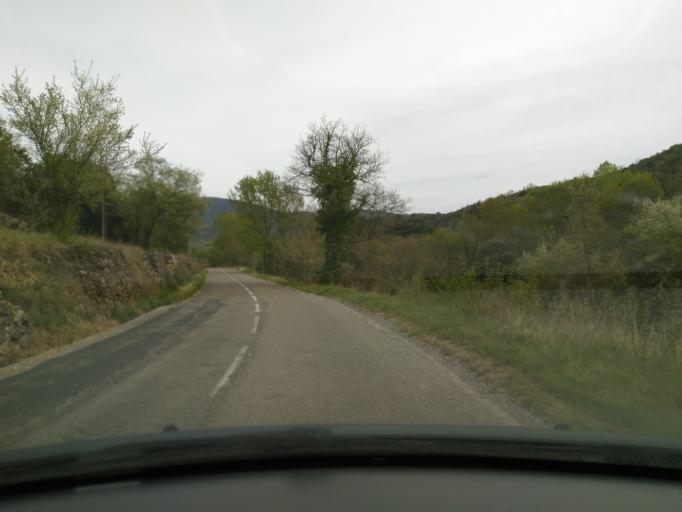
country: FR
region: Rhone-Alpes
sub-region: Departement de l'Ardeche
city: Ruoms
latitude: 44.4330
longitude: 4.4117
